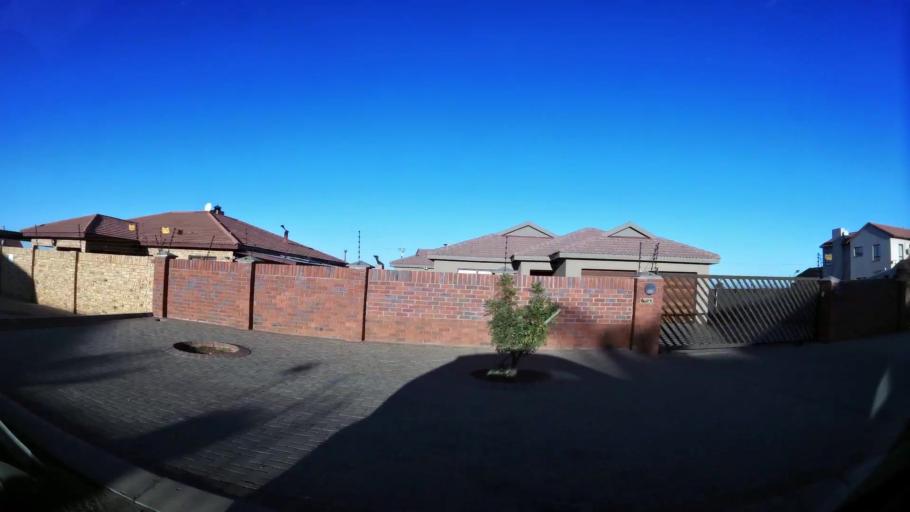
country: ZA
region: Northern Cape
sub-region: Frances Baard District Municipality
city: Kimberley
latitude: -28.7606
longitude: 24.7360
